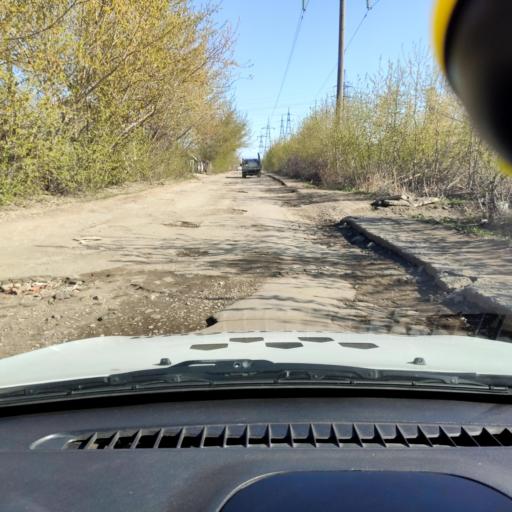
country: RU
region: Samara
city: Tol'yatti
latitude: 53.5857
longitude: 49.2949
